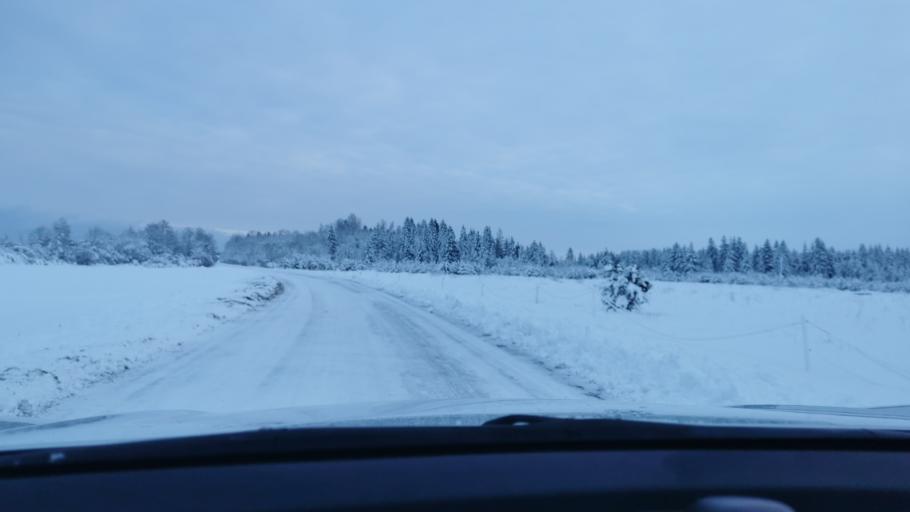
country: EE
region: Laeaene-Virumaa
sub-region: Haljala vald
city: Haljala
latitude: 59.4884
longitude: 26.3848
